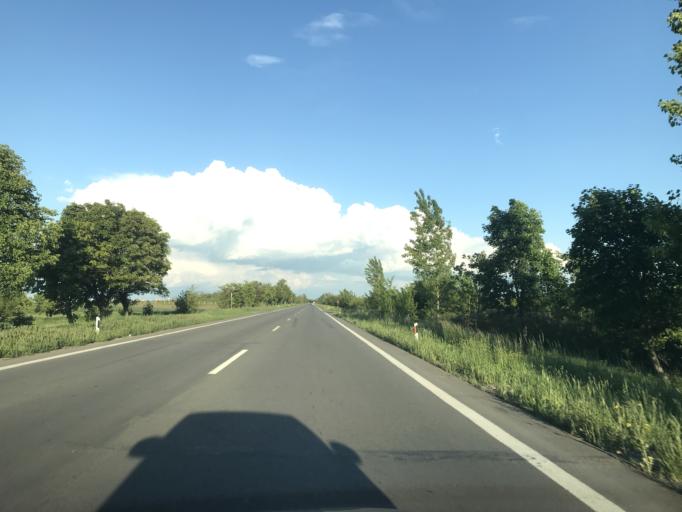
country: RS
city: Aradac
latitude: 45.3871
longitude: 20.3156
